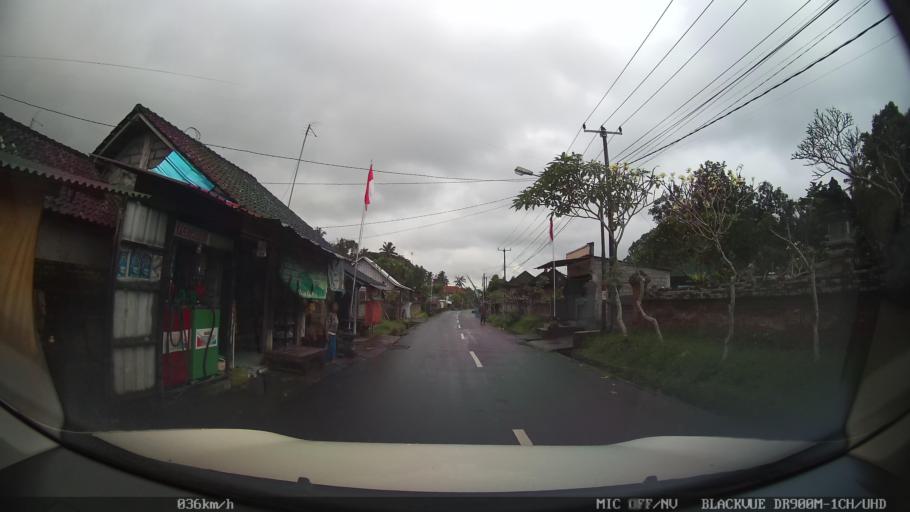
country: ID
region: Bali
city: Banjar Teguan
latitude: -8.4950
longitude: 115.2387
